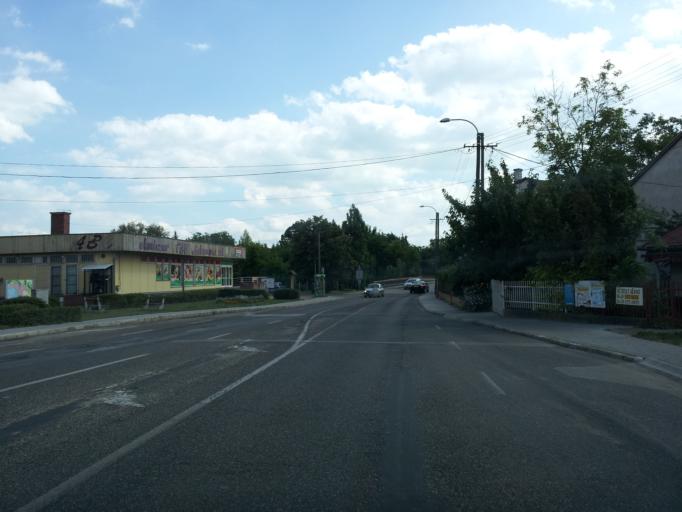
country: HU
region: Veszprem
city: Balatonalmadi
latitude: 47.0439
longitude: 18.0096
